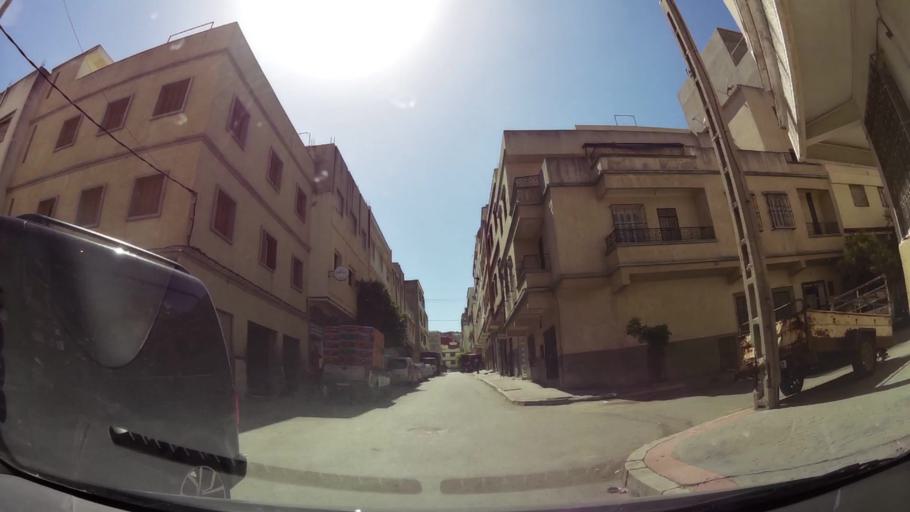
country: MA
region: Tanger-Tetouan
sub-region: Tanger-Assilah
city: Tangier
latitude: 35.7501
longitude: -5.8097
